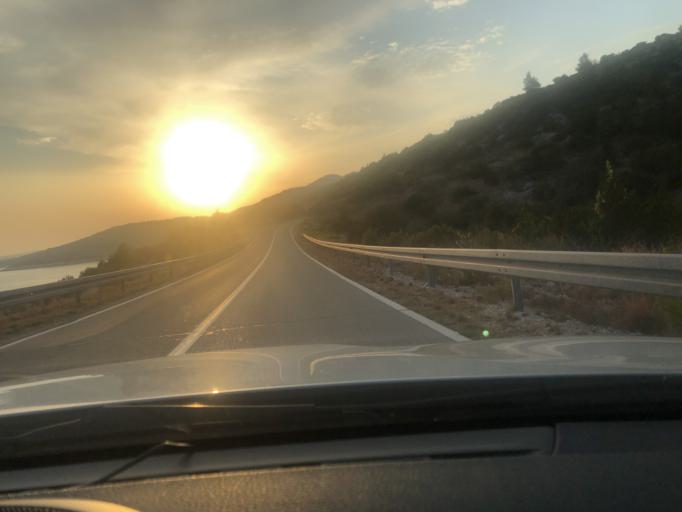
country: HR
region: Splitsko-Dalmatinska
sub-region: Grad Hvar
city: Hvar
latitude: 43.1578
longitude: 16.5027
